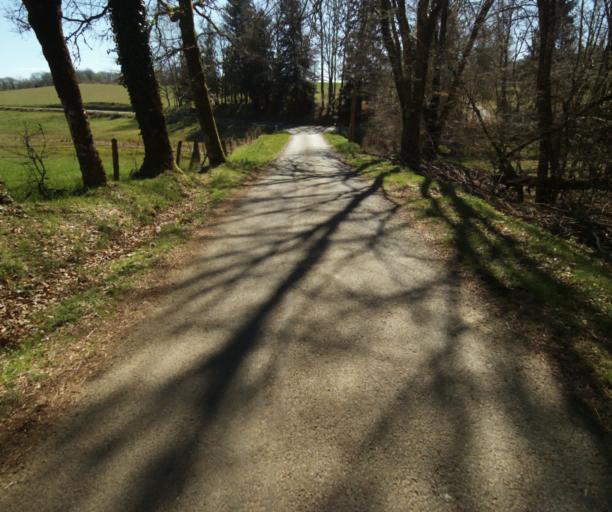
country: FR
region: Limousin
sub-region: Departement de la Correze
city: Chamboulive
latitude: 45.4159
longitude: 1.7304
